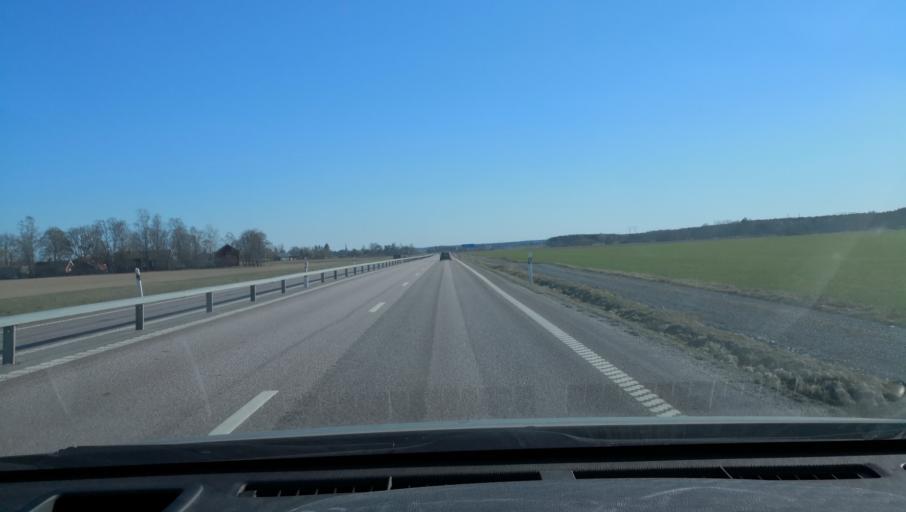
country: SE
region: Vaestmanland
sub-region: Vasteras
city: Tillberga
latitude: 59.7609
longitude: 16.5574
